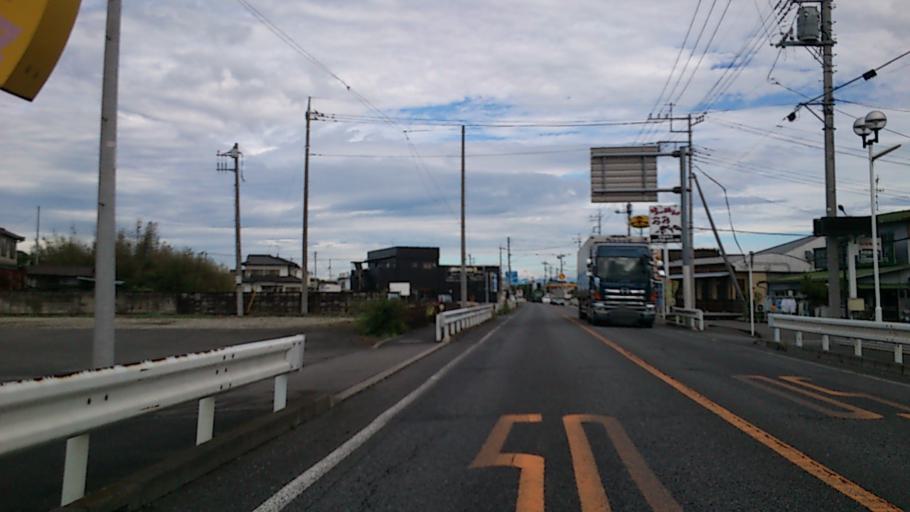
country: JP
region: Saitama
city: Honjo
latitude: 36.2591
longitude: 139.1498
